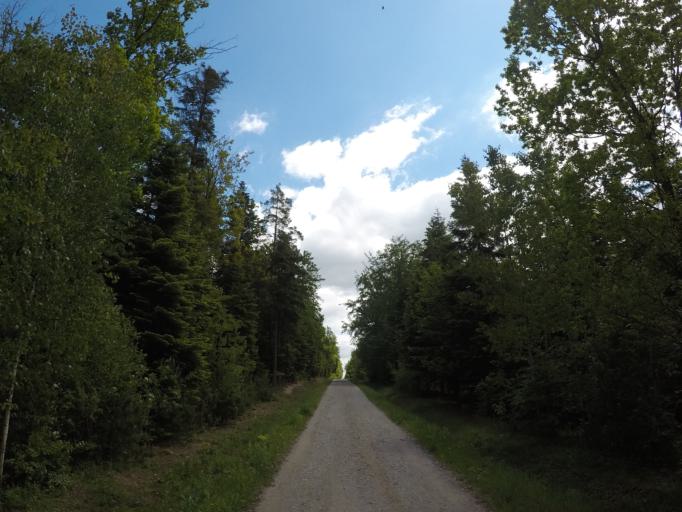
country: PL
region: Swietokrzyskie
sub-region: Powiat kielecki
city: Kielce
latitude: 50.9165
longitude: 20.6444
